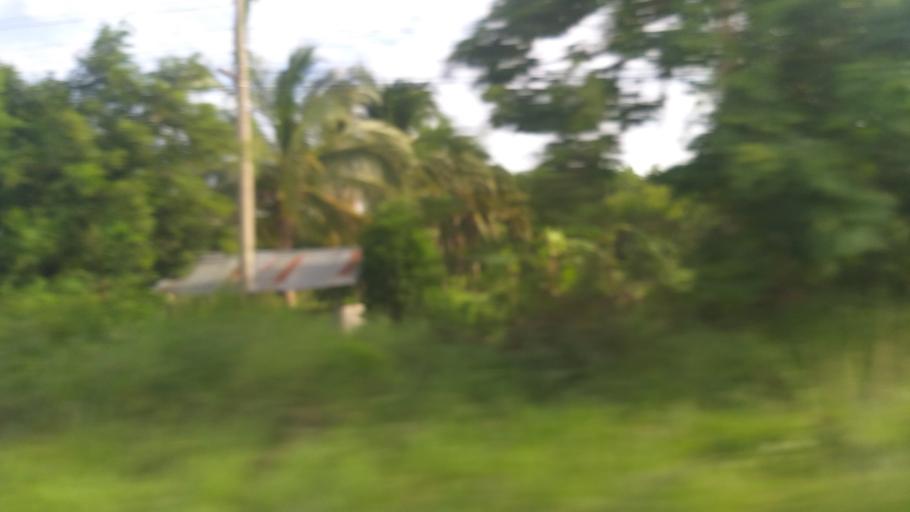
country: TH
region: Chaiyaphum
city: Ban Thaen
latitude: 16.3812
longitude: 102.2989
